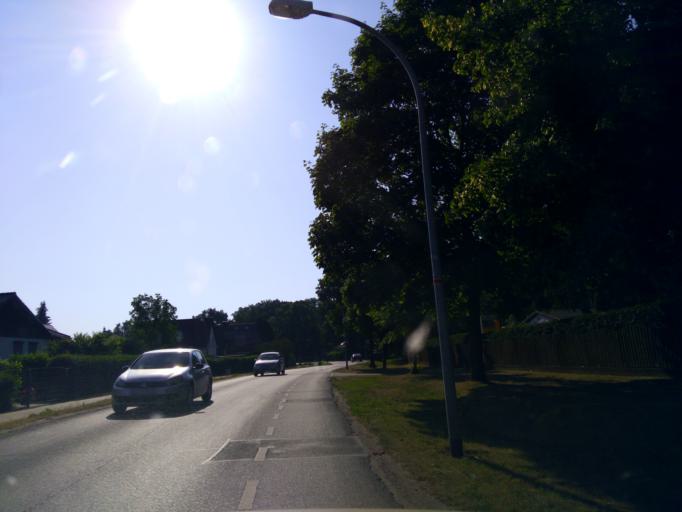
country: DE
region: Brandenburg
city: Dallgow-Doeberitz
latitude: 52.5605
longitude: 13.0470
